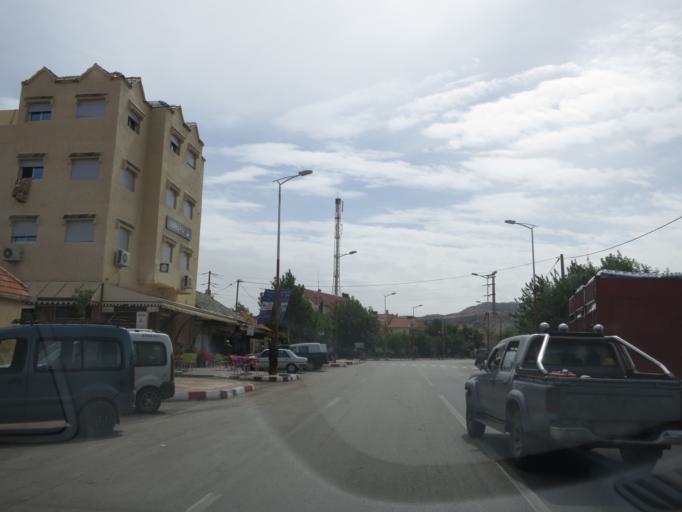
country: MA
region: Meknes-Tafilalet
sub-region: Ifrane
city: Azrou
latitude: 33.2375
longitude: -5.0606
